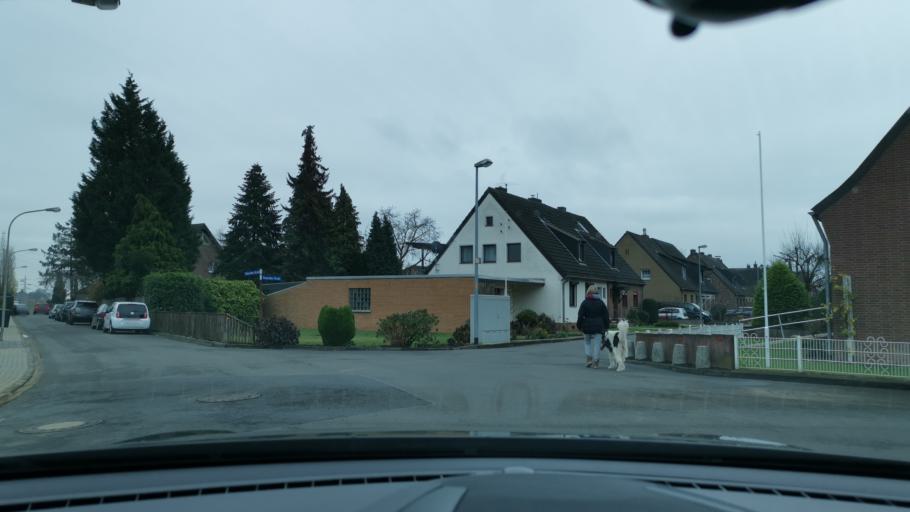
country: DE
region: North Rhine-Westphalia
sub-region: Regierungsbezirk Dusseldorf
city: Neubrueck
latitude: 51.1210
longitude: 6.6884
